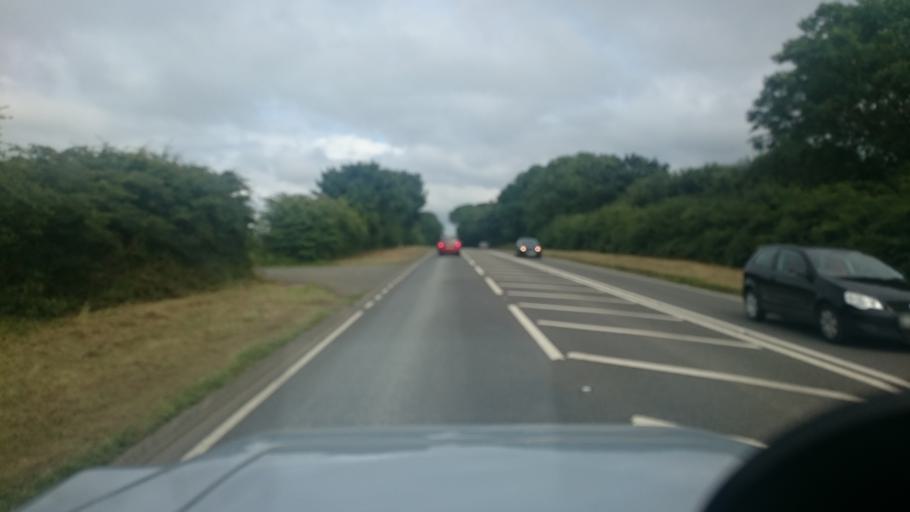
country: GB
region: Wales
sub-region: Pembrokeshire
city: Wiston
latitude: 51.8045
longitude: -4.8833
